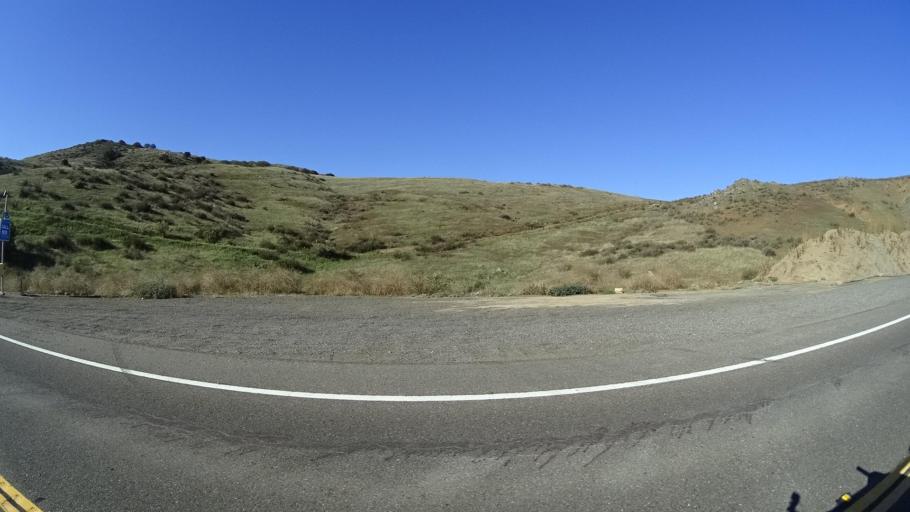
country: US
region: California
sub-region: San Diego County
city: Jamul
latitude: 32.6789
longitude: -116.8398
